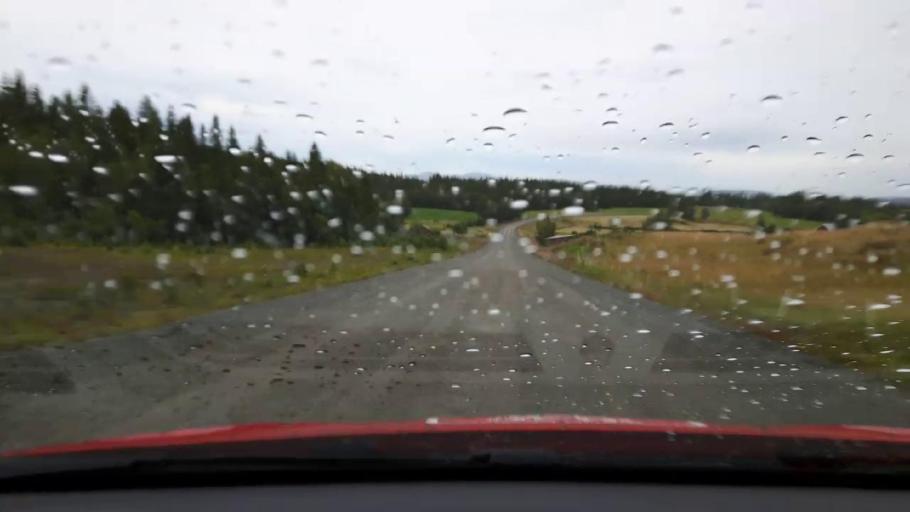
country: SE
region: Jaemtland
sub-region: Are Kommun
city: Are
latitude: 63.4730
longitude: 12.5655
